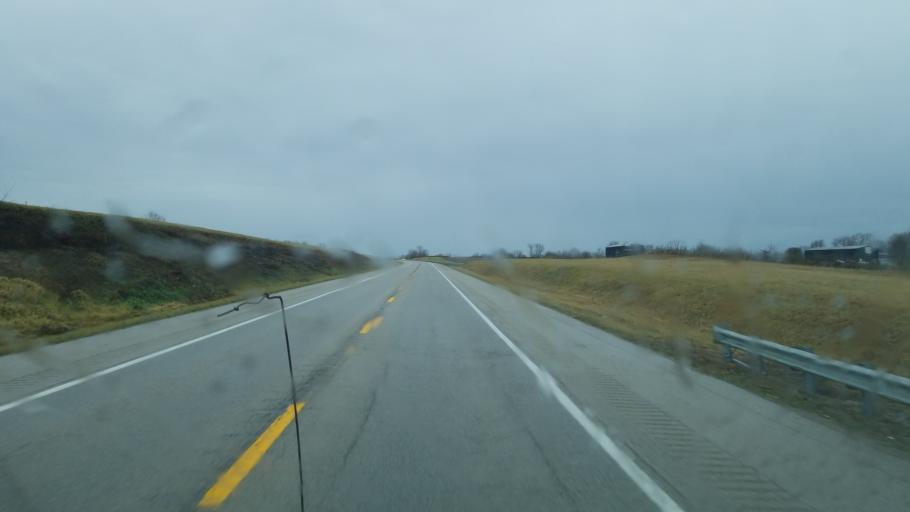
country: US
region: Ohio
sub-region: Adams County
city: Manchester
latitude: 38.5639
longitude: -83.6206
